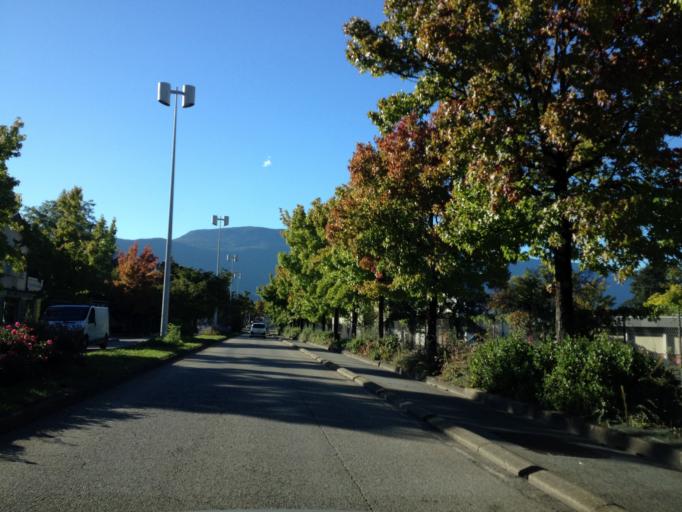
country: FR
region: Rhone-Alpes
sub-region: Departement de la Savoie
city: Cognin
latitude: 45.5750
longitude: 5.9016
